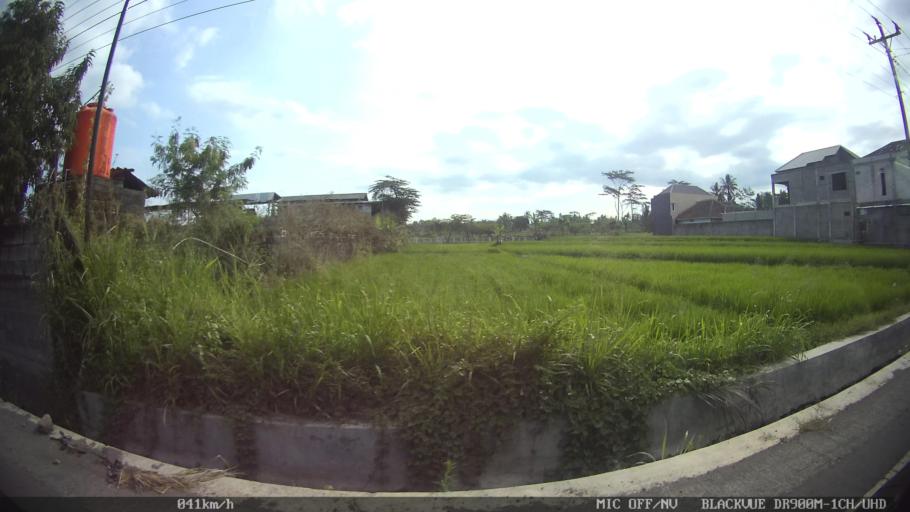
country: ID
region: Central Java
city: Candi Prambanan
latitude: -7.6846
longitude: 110.4604
